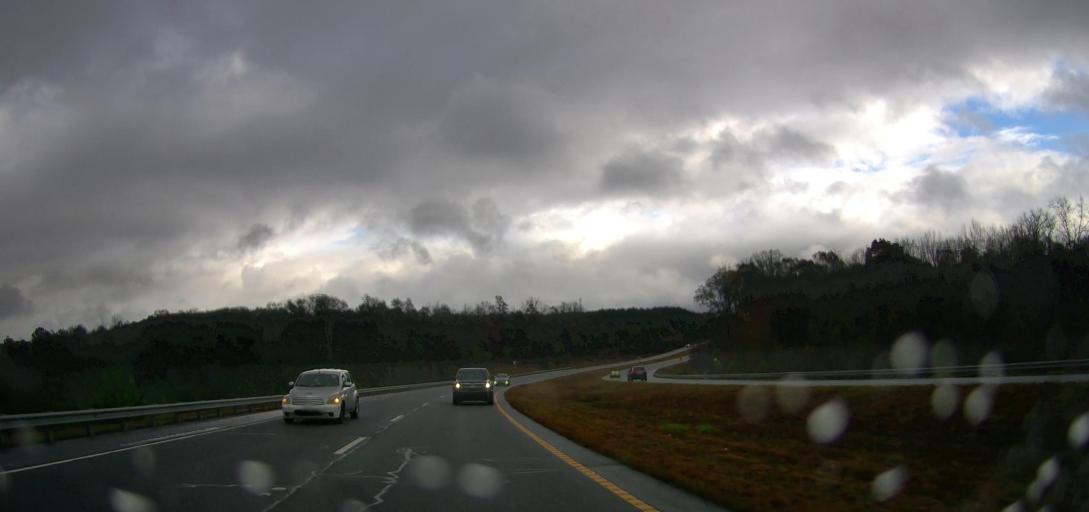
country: US
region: Georgia
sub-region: Jackson County
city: Nicholson
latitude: 34.0597
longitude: -83.4148
